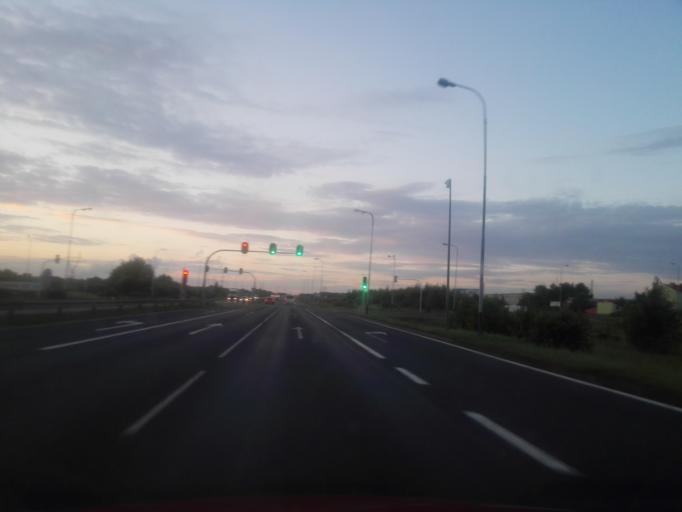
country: PL
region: Lodz Voivodeship
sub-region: Powiat radomszczanski
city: Radomsko
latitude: 51.0790
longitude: 19.3718
